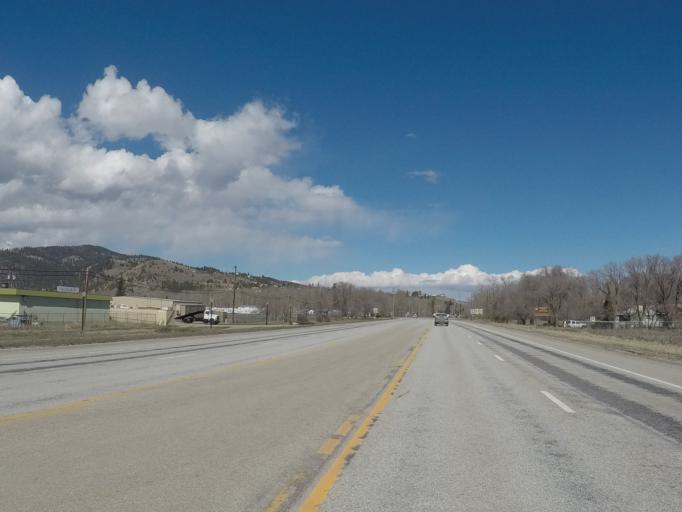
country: US
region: Montana
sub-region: Missoula County
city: Lolo
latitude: 46.7450
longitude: -114.0820
